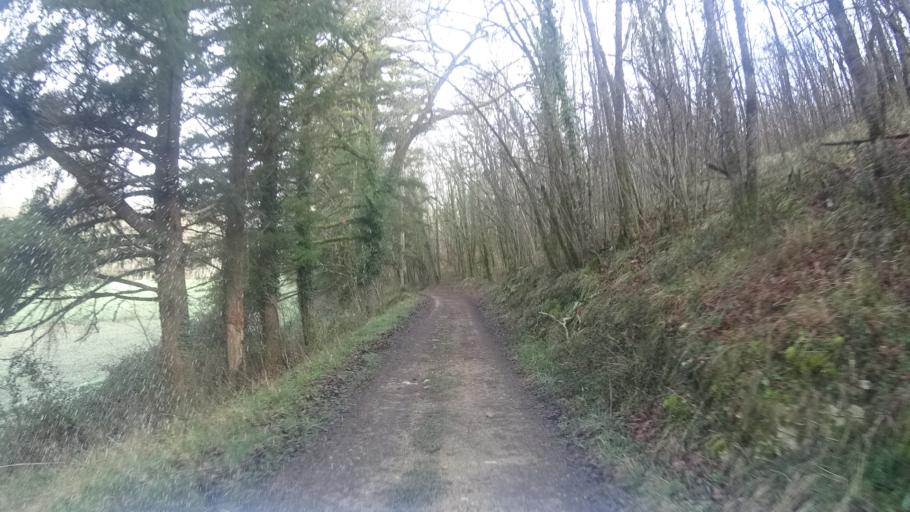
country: FR
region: Aquitaine
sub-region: Departement de la Dordogne
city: Terrasson-Lavilledieu
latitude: 45.0948
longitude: 1.2635
